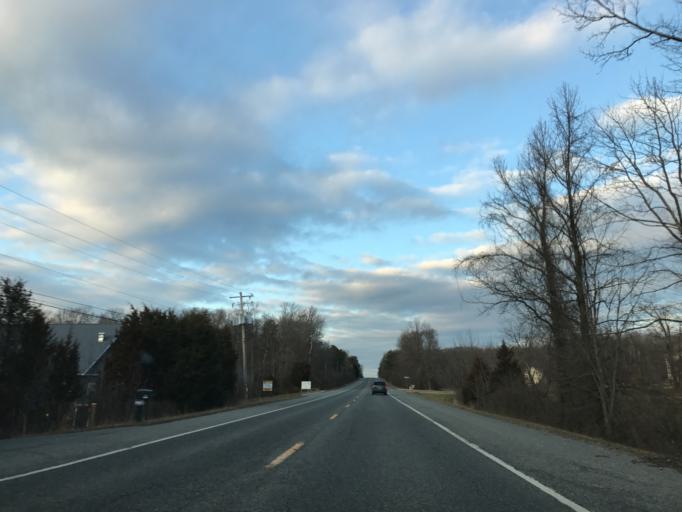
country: US
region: Maryland
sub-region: Cecil County
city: Charlestown
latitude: 39.5623
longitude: -75.9488
